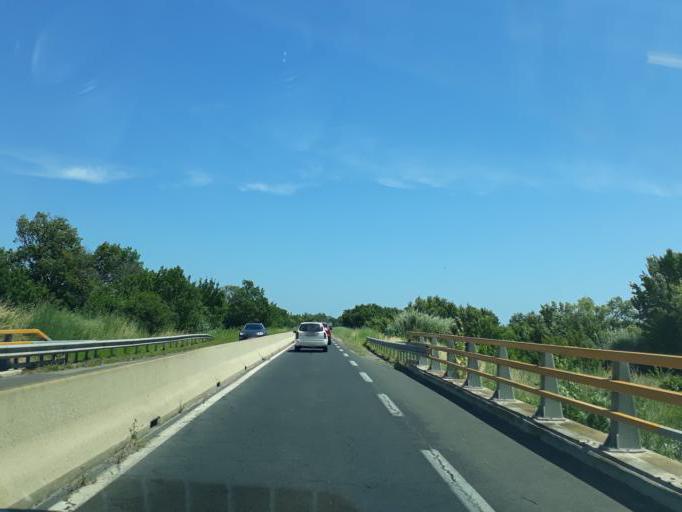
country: FR
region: Languedoc-Roussillon
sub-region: Departement de l'Herault
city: Vias
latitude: 43.3080
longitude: 3.4092
